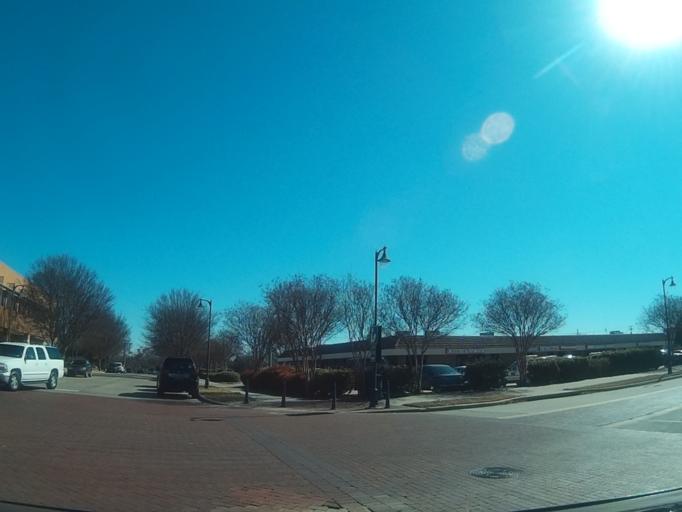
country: US
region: Texas
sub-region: Collin County
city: Allen
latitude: 33.1049
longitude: -96.6716
